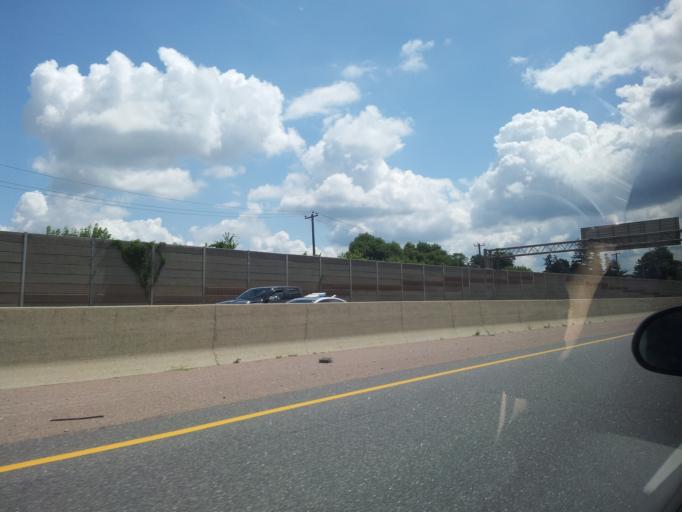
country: CA
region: Ontario
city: Kitchener
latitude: 43.4512
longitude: -80.4652
